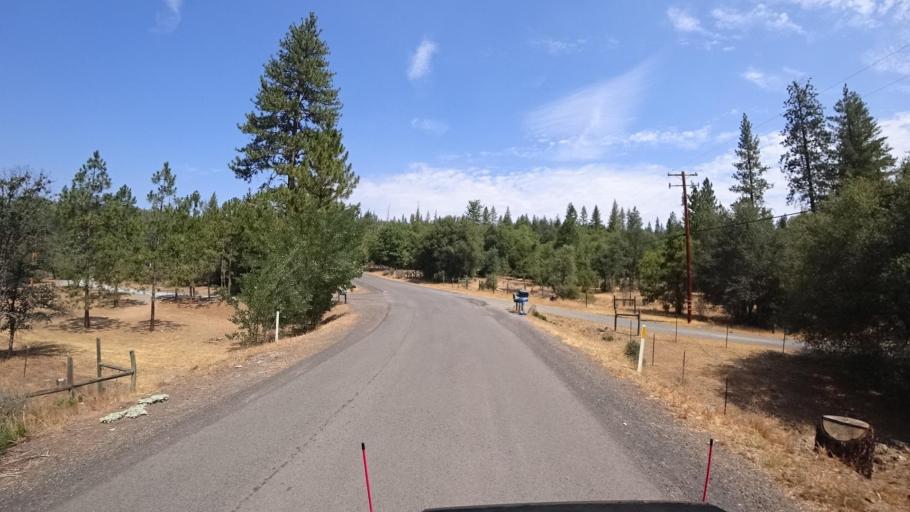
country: US
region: California
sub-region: Mariposa County
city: Midpines
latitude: 37.7023
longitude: -120.0972
